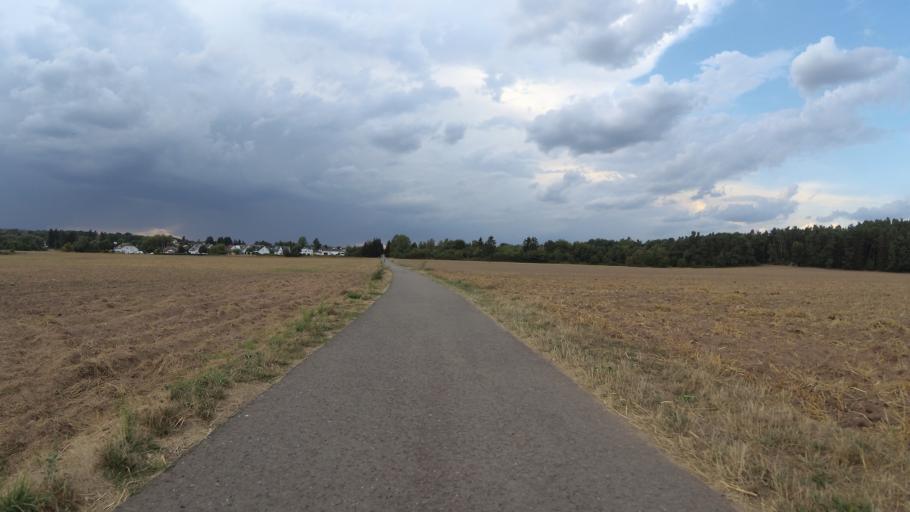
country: DE
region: Saarland
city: Bexbach
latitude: 49.3201
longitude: 7.2508
